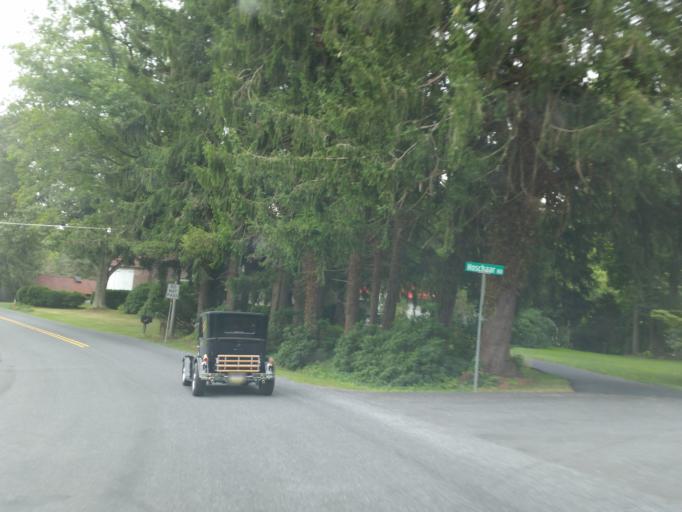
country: US
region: Pennsylvania
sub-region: Berks County
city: Alleghenyville
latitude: 40.2333
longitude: -75.9881
